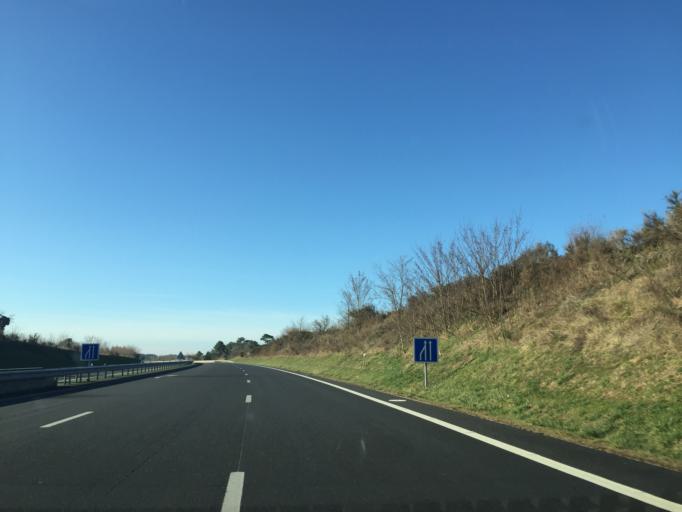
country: FR
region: Limousin
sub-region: Departement de la Correze
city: Cublac
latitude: 45.1724
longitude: 1.3187
